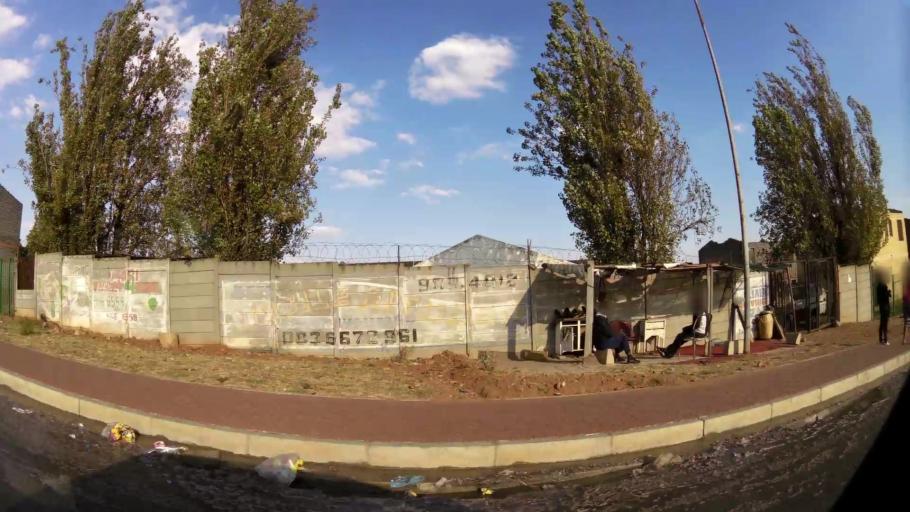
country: ZA
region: Gauteng
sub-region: City of Johannesburg Metropolitan Municipality
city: Soweto
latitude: -26.2322
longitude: 27.8954
